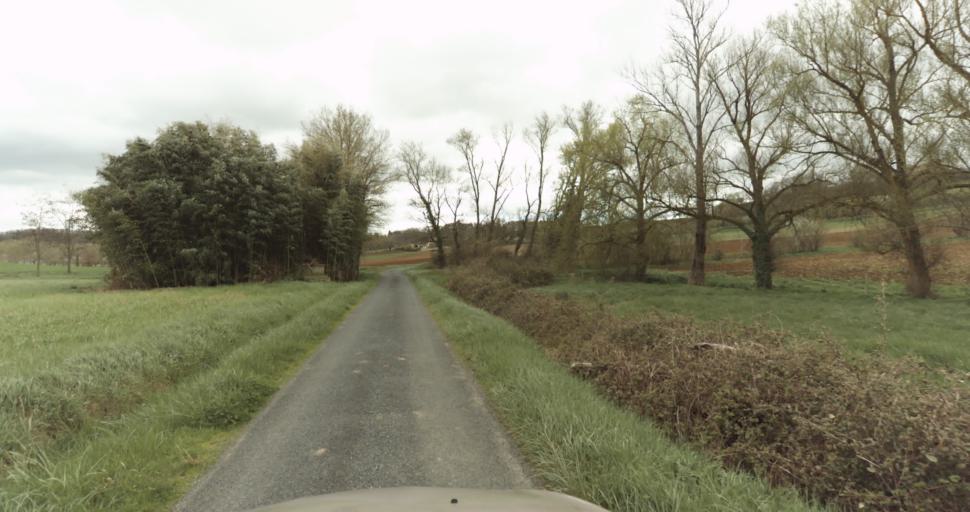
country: FR
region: Midi-Pyrenees
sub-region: Departement du Tarn
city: Puygouzon
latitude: 43.8741
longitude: 2.1731
